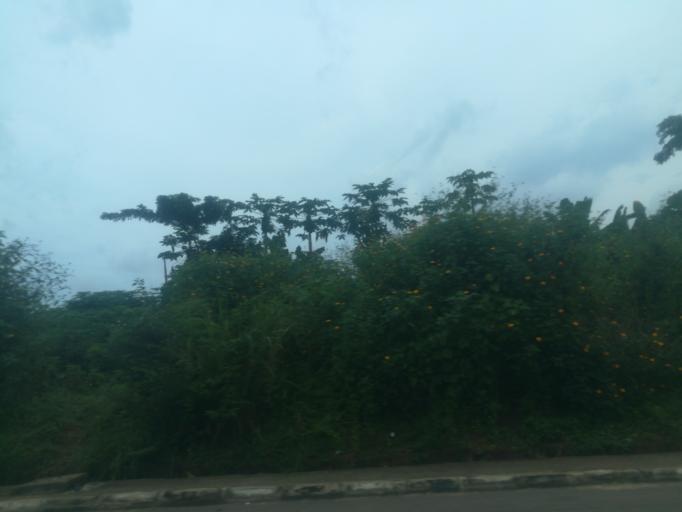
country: NG
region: Oyo
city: Ibadan
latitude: 7.3800
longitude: 3.8287
